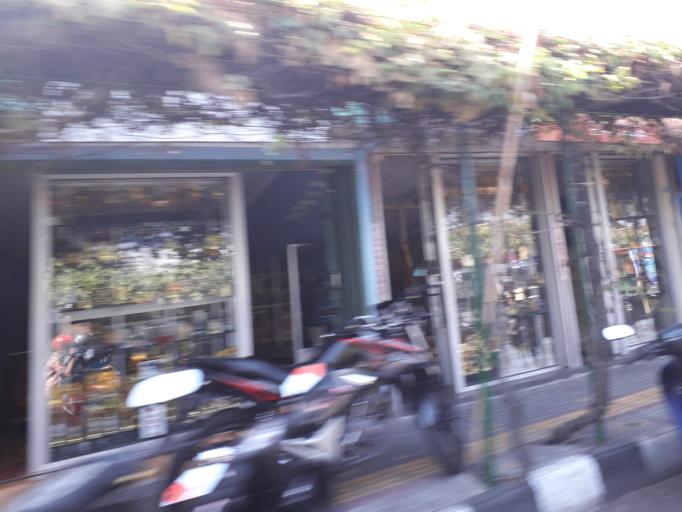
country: ID
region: Daerah Istimewa Yogyakarta
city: Yogyakarta
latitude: -7.7944
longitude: 110.3694
